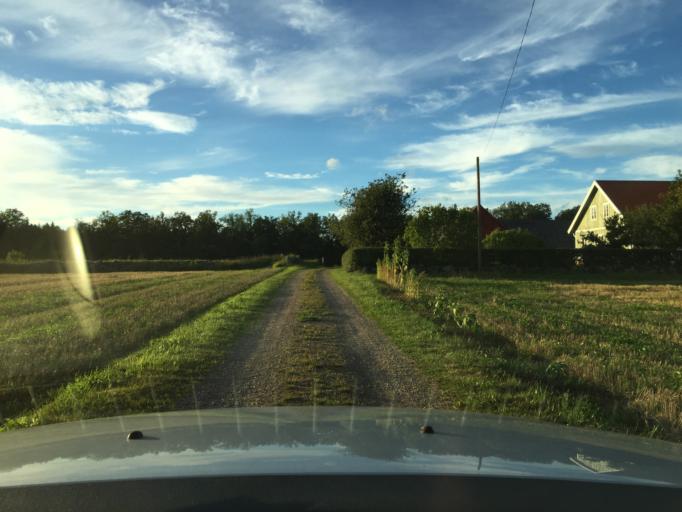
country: SE
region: Skane
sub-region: Hassleholms Kommun
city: Sosdala
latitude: 56.0078
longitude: 13.7832
